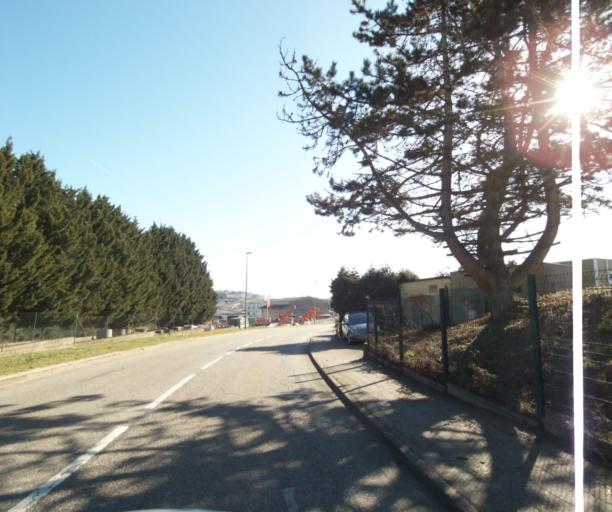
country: FR
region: Lorraine
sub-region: Departement de Meurthe-et-Moselle
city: Vandoeuvre-les-Nancy
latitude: 48.6463
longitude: 6.1855
